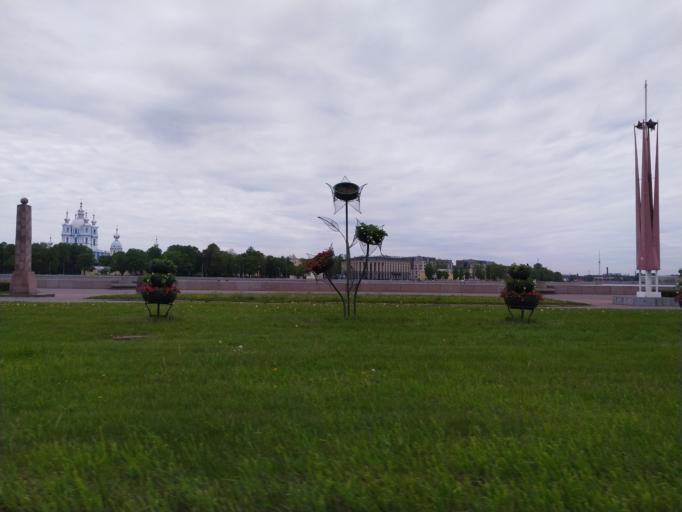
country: RU
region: Leningrad
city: Finlyandskiy
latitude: 59.9512
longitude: 30.4070
